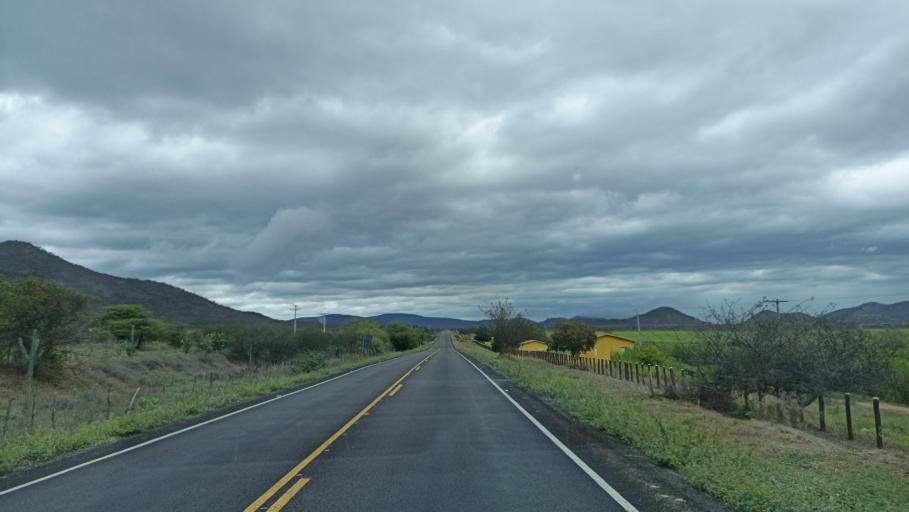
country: BR
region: Bahia
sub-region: Iacu
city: Iacu
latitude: -12.8913
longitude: -40.3967
